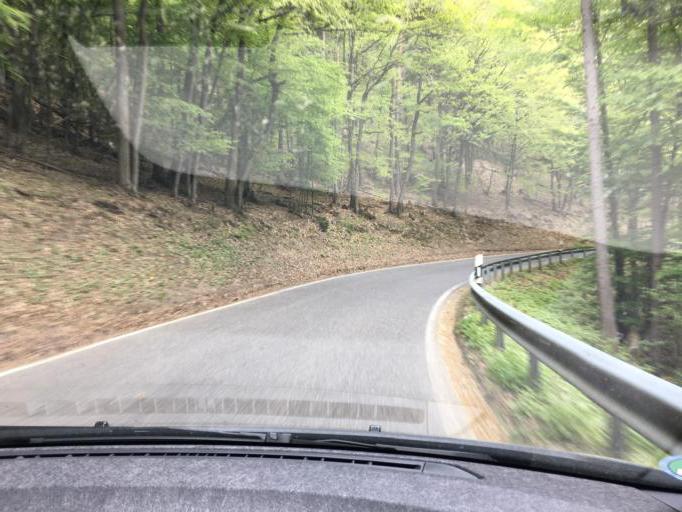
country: DE
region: Rheinland-Pfalz
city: Lind
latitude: 50.4989
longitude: 6.9548
